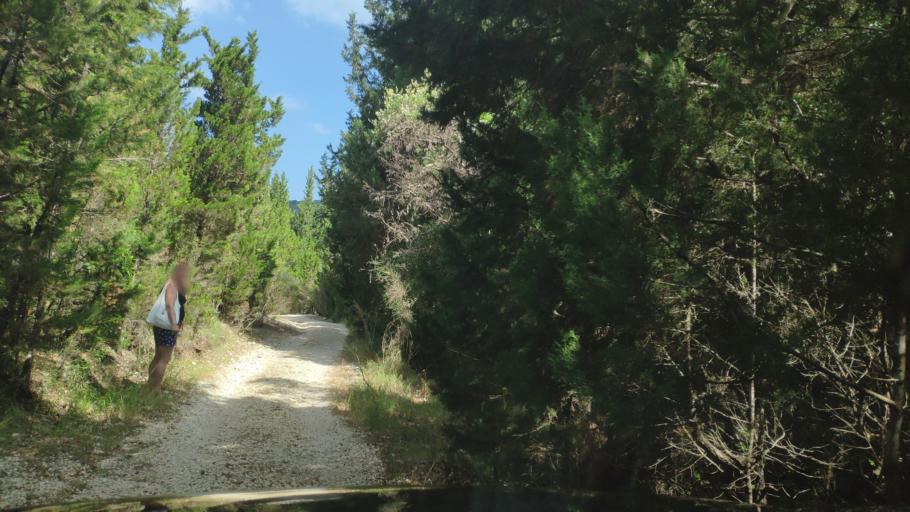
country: GR
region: Ionian Islands
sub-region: Lefkada
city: Lefkada
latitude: 38.7978
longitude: 20.6737
